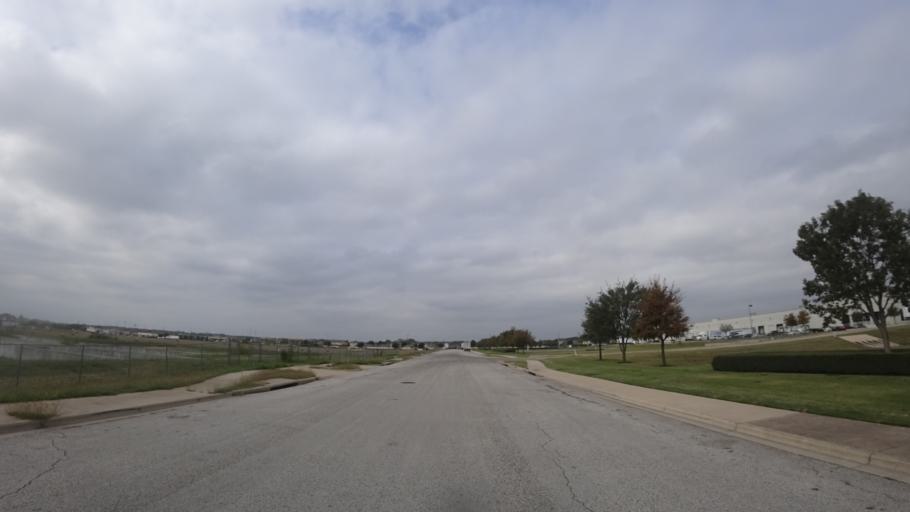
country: US
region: Texas
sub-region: Travis County
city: Manor
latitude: 30.3709
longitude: -97.6090
